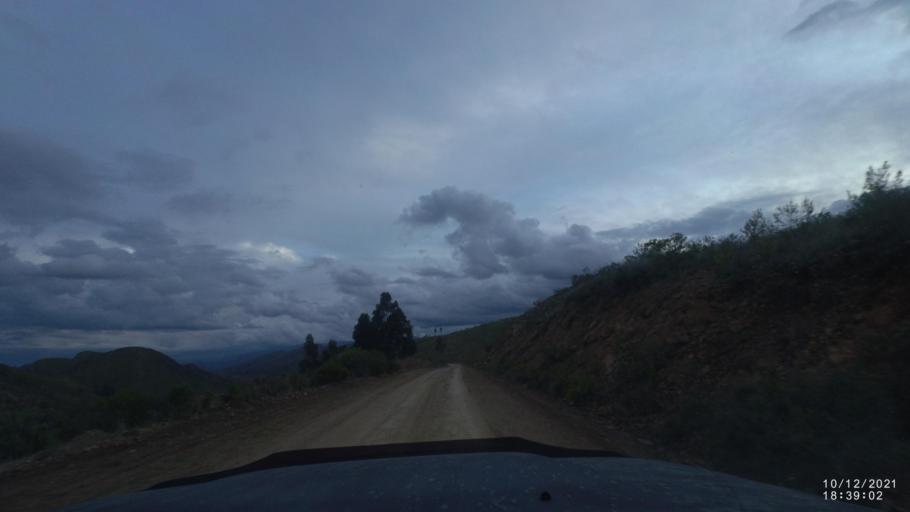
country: BO
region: Cochabamba
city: Tarata
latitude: -17.8467
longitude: -65.9894
